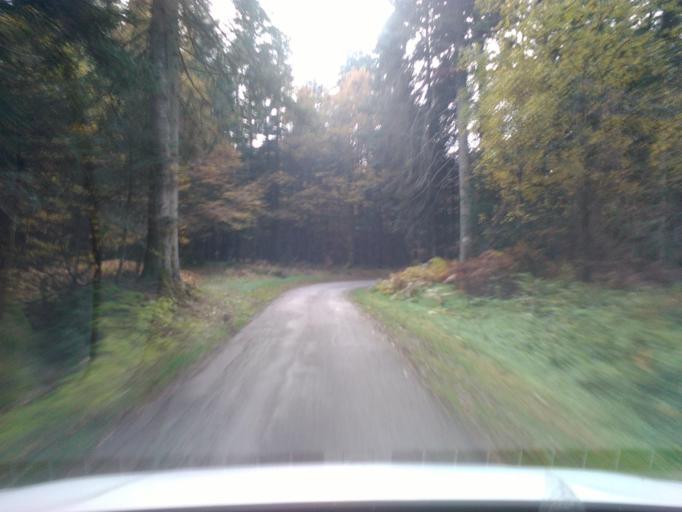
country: FR
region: Lorraine
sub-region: Departement des Vosges
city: Moyenmoutier
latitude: 48.3542
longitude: 6.9025
